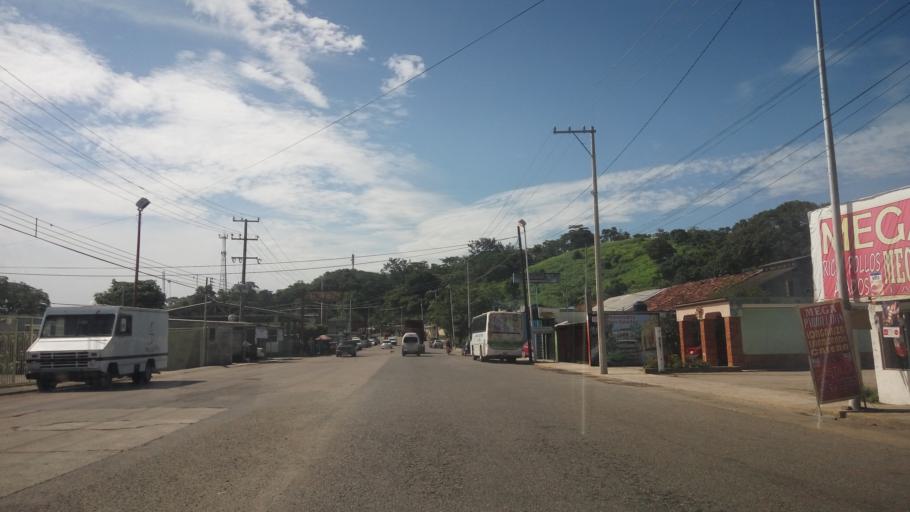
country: MX
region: Tabasco
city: Teapa
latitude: 17.5683
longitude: -92.9553
